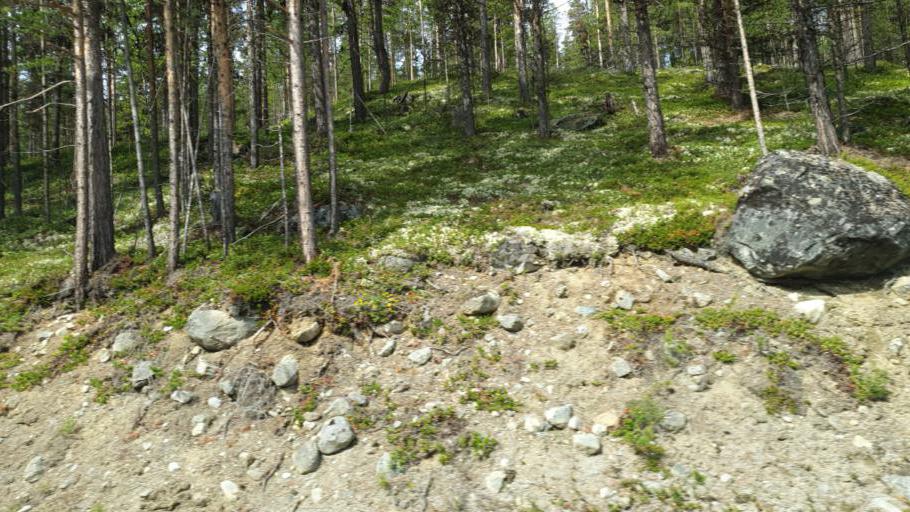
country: NO
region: Oppland
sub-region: Vaga
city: Vagamo
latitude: 61.6776
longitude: 9.0487
